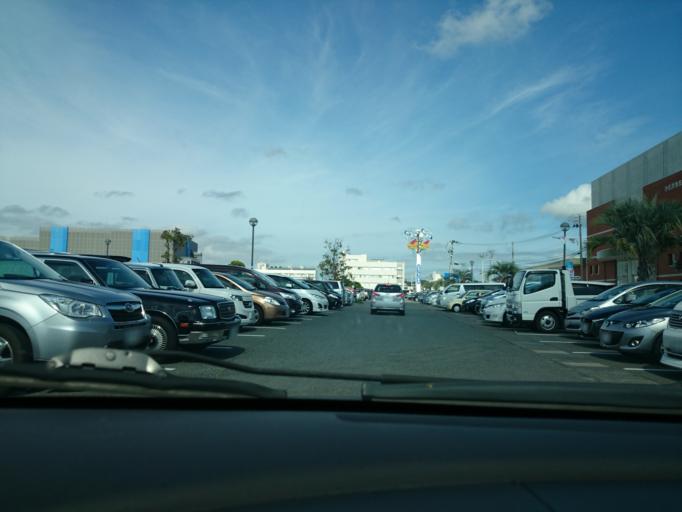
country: JP
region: Fukushima
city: Iwaki
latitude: 36.9440
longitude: 140.9063
